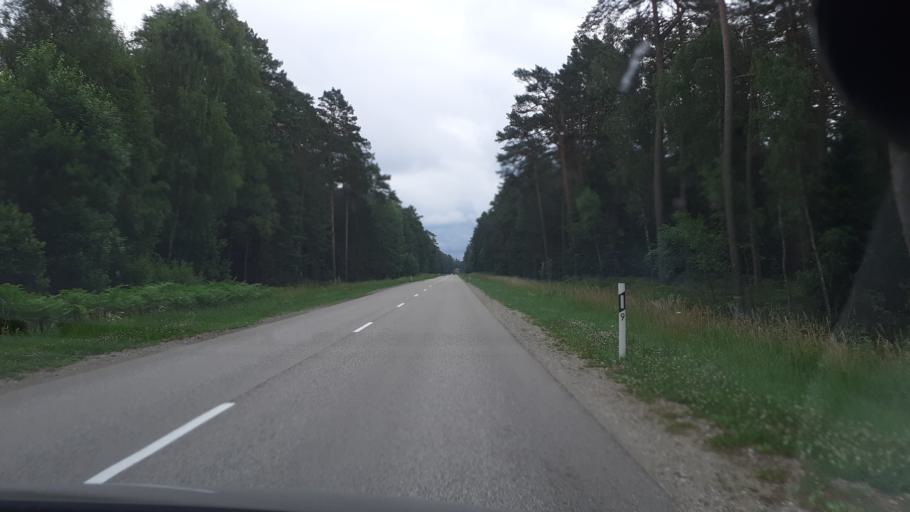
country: LV
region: Ventspils Rajons
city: Piltene
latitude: 57.1123
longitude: 21.7601
